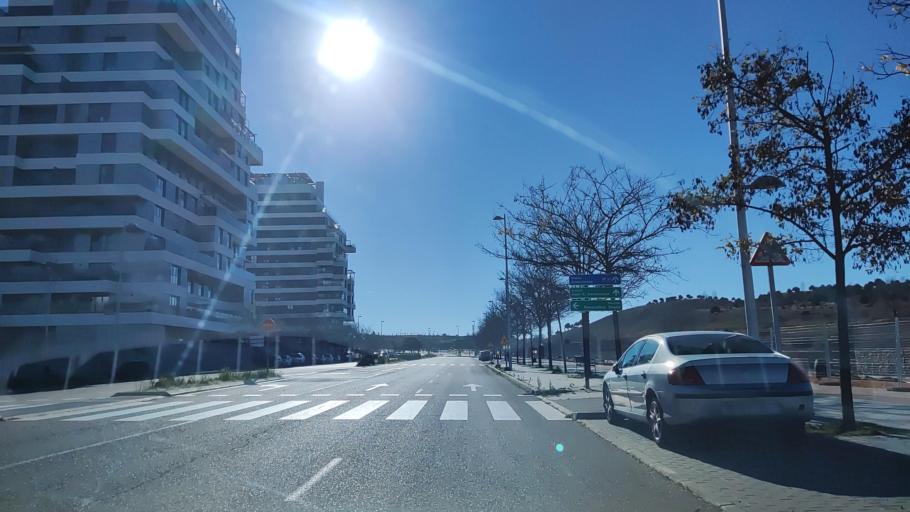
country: ES
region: Madrid
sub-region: Provincia de Madrid
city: Hortaleza
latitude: 40.4959
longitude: -3.6239
